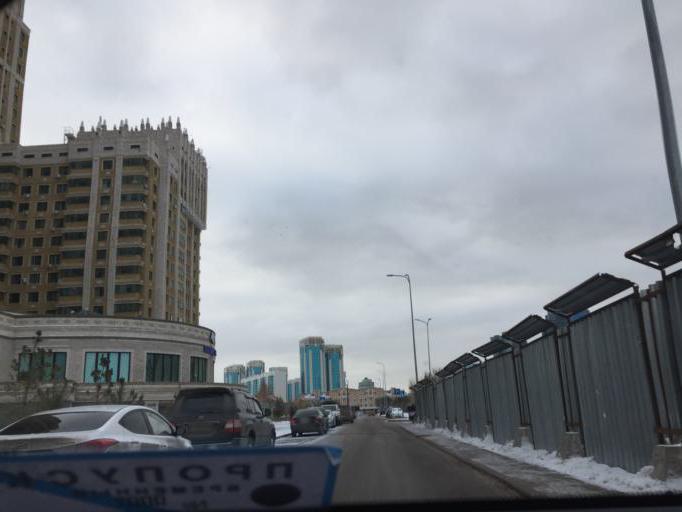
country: KZ
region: Astana Qalasy
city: Astana
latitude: 51.1402
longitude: 71.4135
